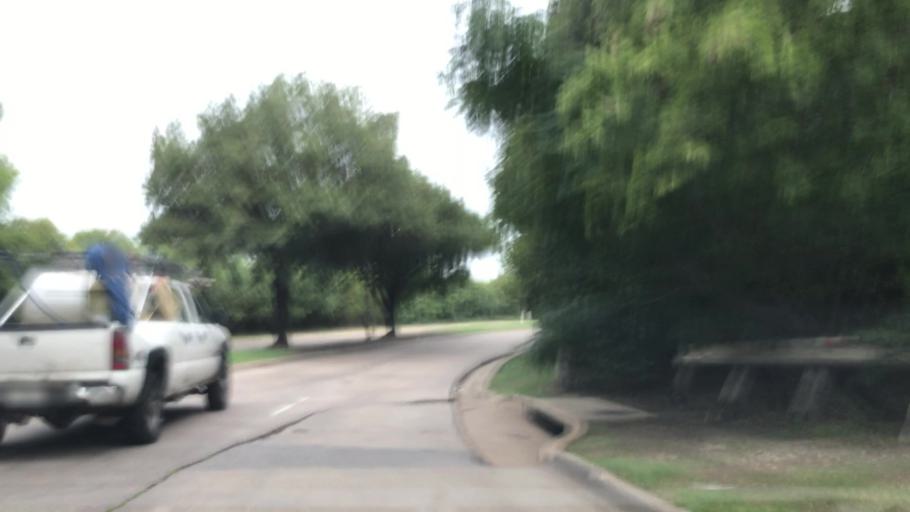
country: US
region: Texas
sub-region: Dallas County
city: Cockrell Hill
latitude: 32.7710
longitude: -96.8762
